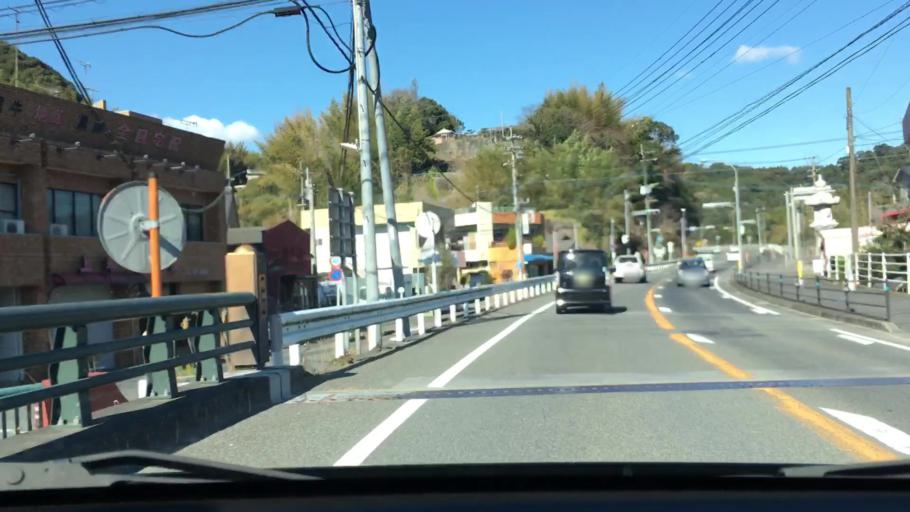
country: JP
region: Kagoshima
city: Ijuin
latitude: 31.6566
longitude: 130.4960
